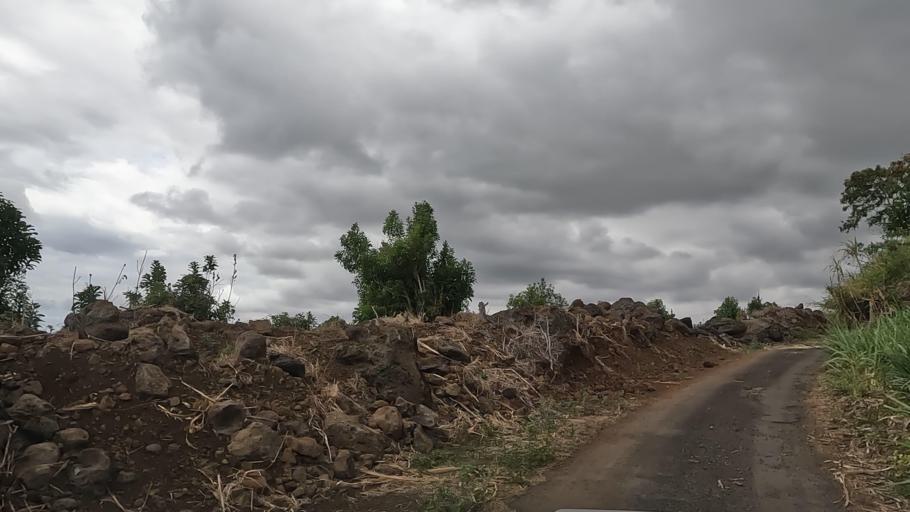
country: RE
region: Reunion
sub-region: Reunion
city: Saint-Pierre
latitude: -21.3424
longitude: 55.5193
